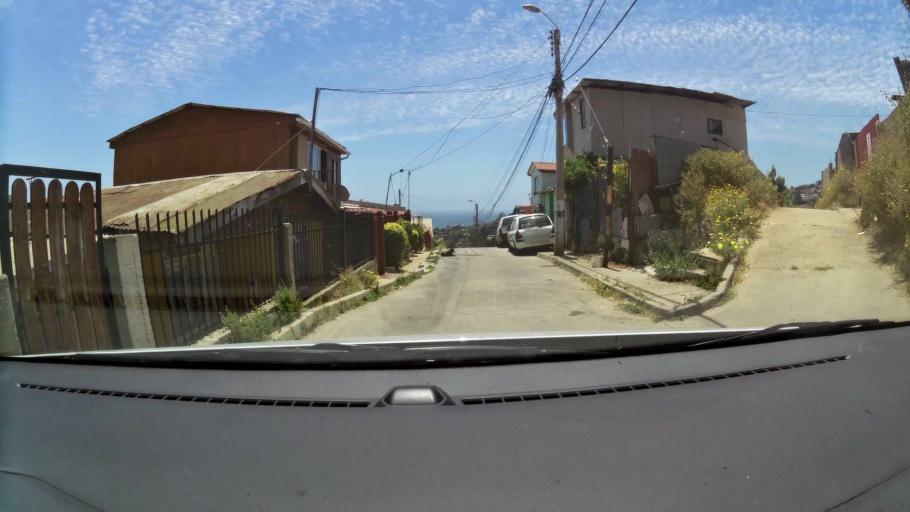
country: CL
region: Valparaiso
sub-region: Provincia de Valparaiso
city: Vina del Mar
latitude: -33.0425
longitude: -71.5858
